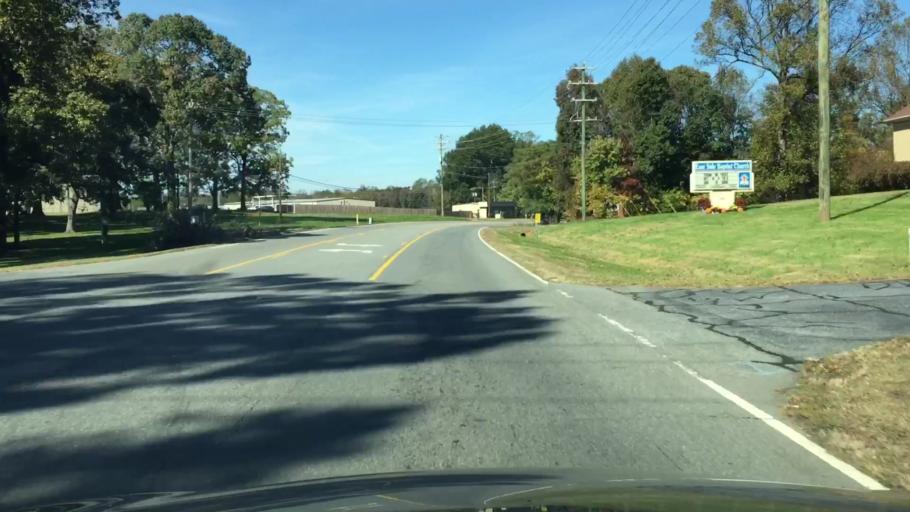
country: US
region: North Carolina
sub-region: Rockingham County
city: Reidsville
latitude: 36.3314
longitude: -79.6501
